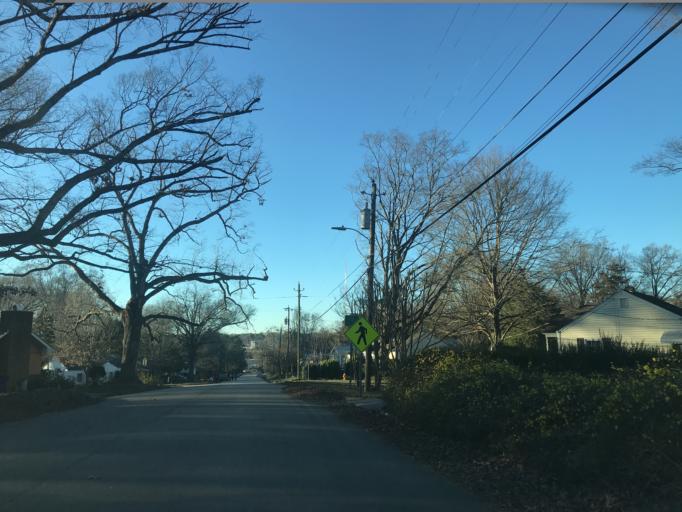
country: US
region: North Carolina
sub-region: Wake County
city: Raleigh
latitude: 35.7989
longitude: -78.6179
